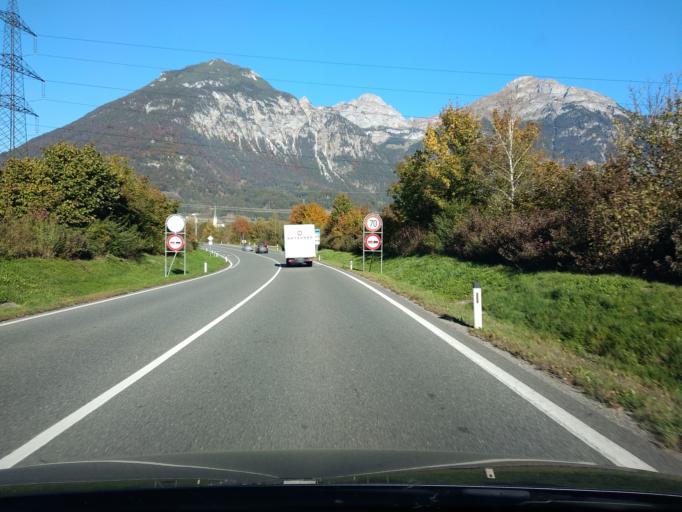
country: AT
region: Tyrol
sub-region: Politischer Bezirk Schwaz
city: Strass im Zillertal
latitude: 47.3958
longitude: 11.8095
